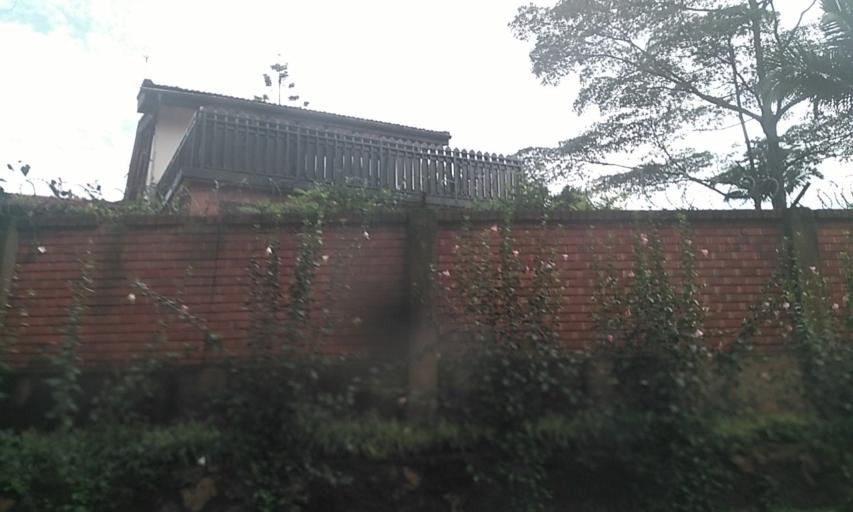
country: UG
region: Central Region
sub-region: Kampala District
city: Kampala
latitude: 0.3245
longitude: 32.5916
